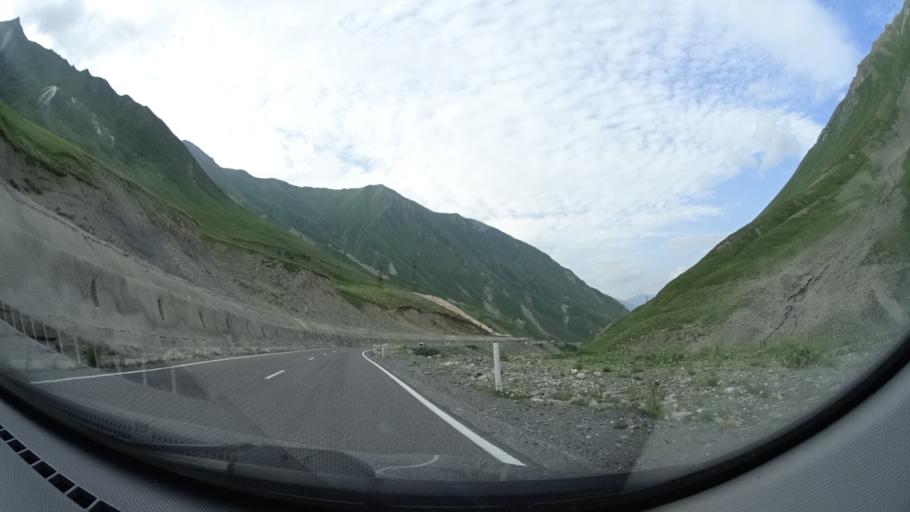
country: GE
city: Gudauri
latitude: 42.5280
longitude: 44.4698
